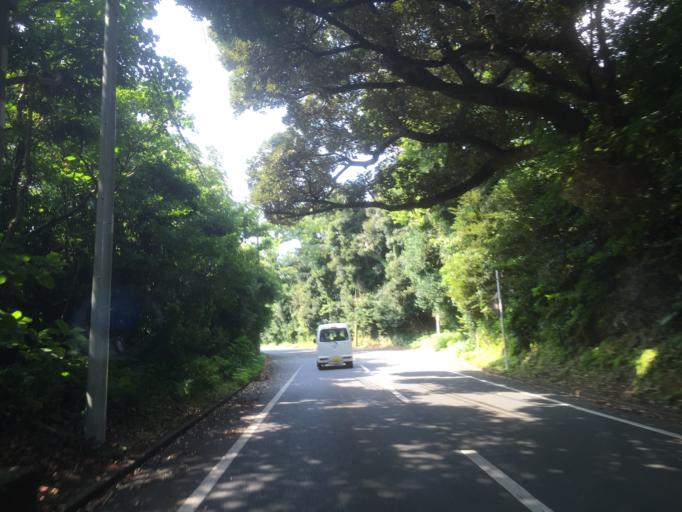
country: JP
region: Shizuoka
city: Shimoda
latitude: 34.0546
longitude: 139.5327
